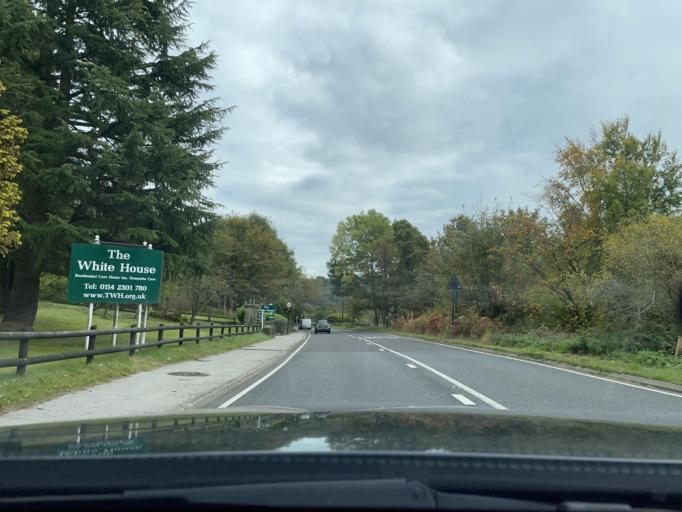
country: GB
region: England
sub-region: Sheffield
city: Bradfield
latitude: 53.3793
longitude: -1.5884
